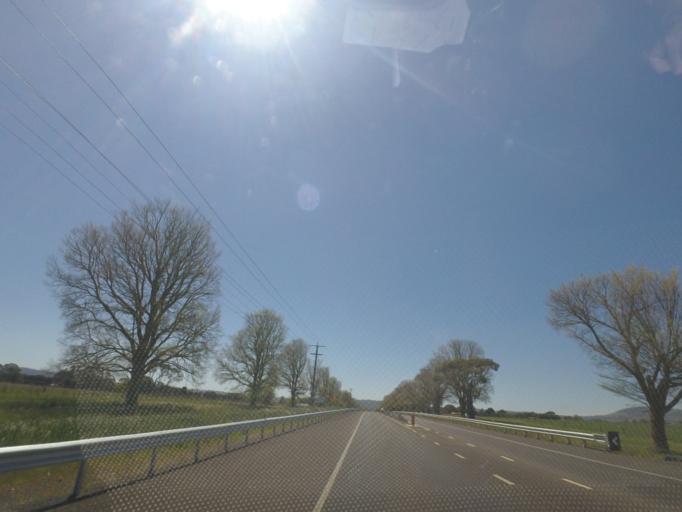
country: AU
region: Victoria
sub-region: Hume
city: Sunbury
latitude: -37.2896
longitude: 144.7368
